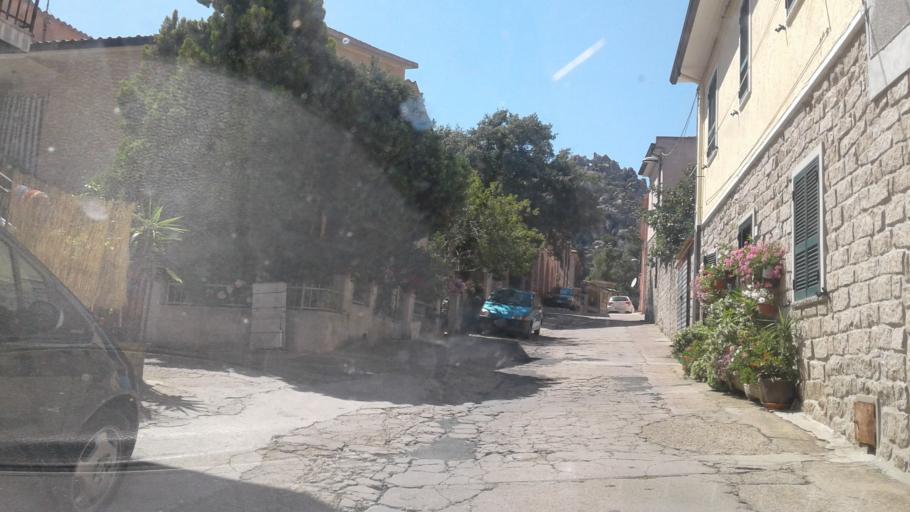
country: IT
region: Sardinia
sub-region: Provincia di Olbia-Tempio
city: Aggius
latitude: 40.9311
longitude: 9.0679
